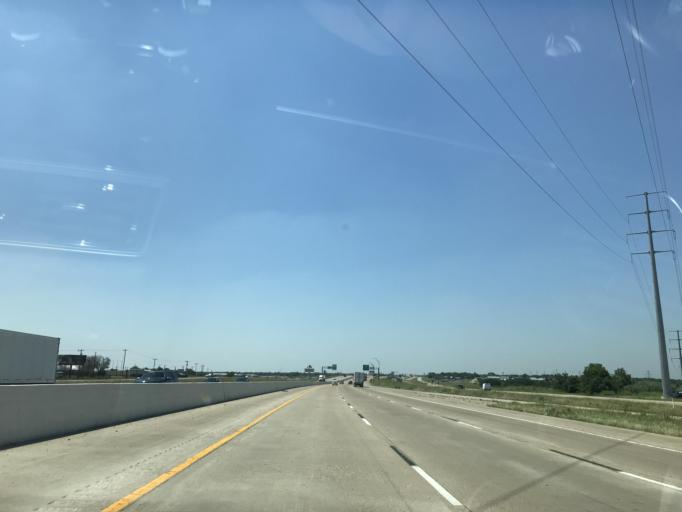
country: US
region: Texas
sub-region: McLennan County
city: Northcrest
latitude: 31.6942
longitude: -97.1016
